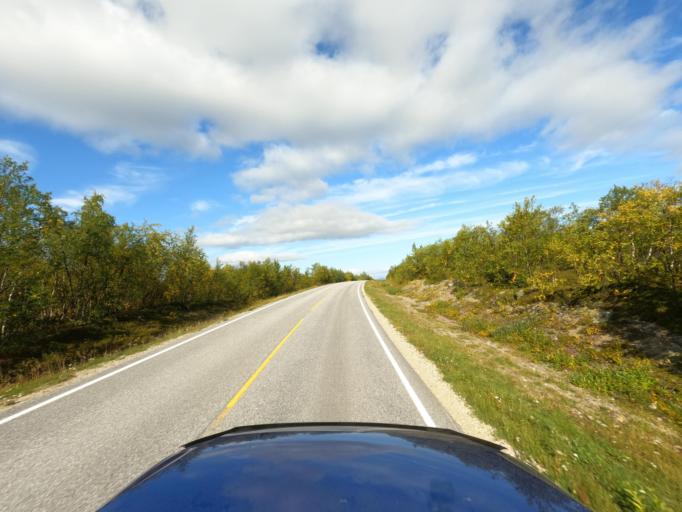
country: NO
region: Finnmark Fylke
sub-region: Karasjok
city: Karasjohka
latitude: 69.6160
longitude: 25.3010
